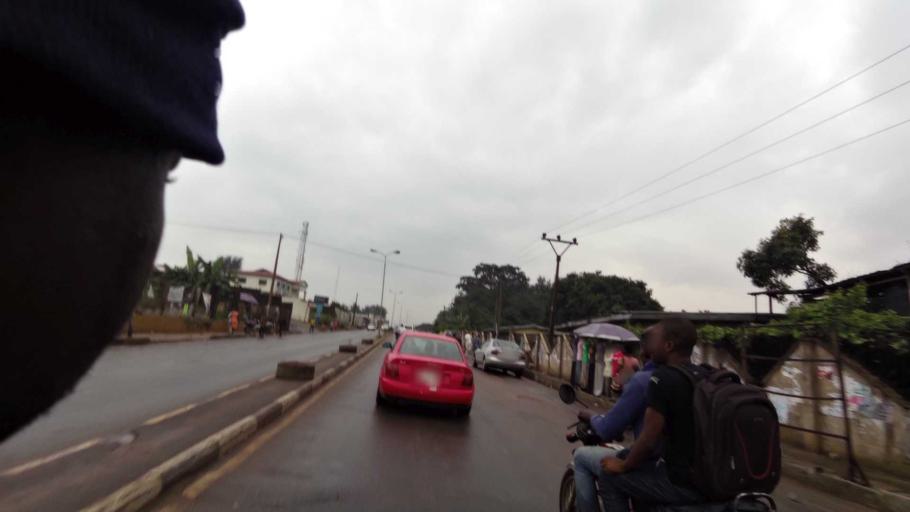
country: NG
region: Oyo
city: Ibadan
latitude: 7.3980
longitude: 3.9214
